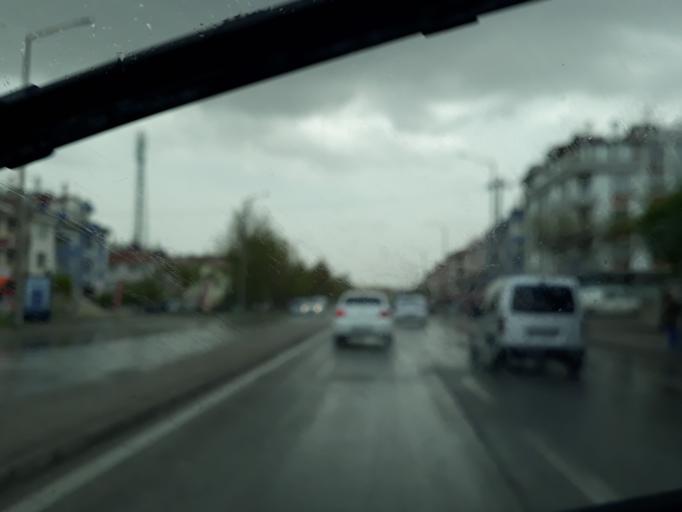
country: TR
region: Konya
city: Selcuklu
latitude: 37.9201
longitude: 32.4925
